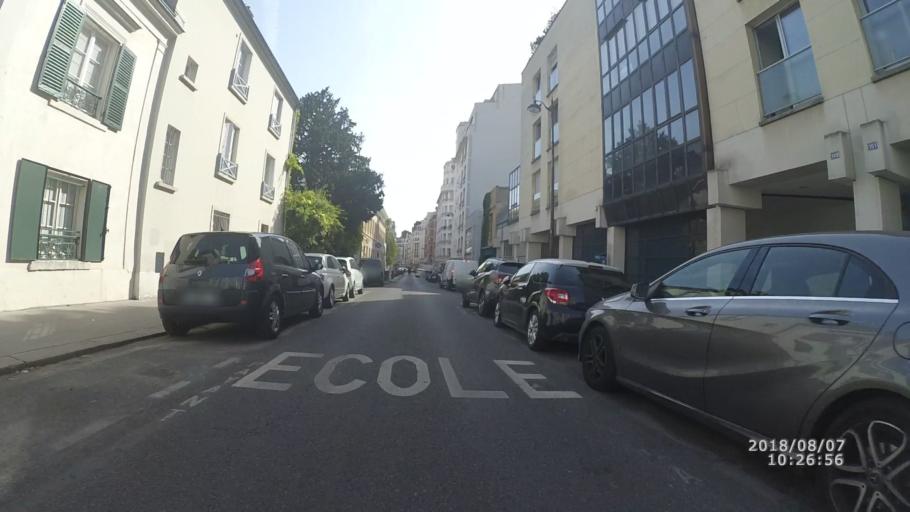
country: FR
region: Ile-de-France
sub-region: Departement du Val-de-Marne
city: Gentilly
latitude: 48.8335
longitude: 2.3428
